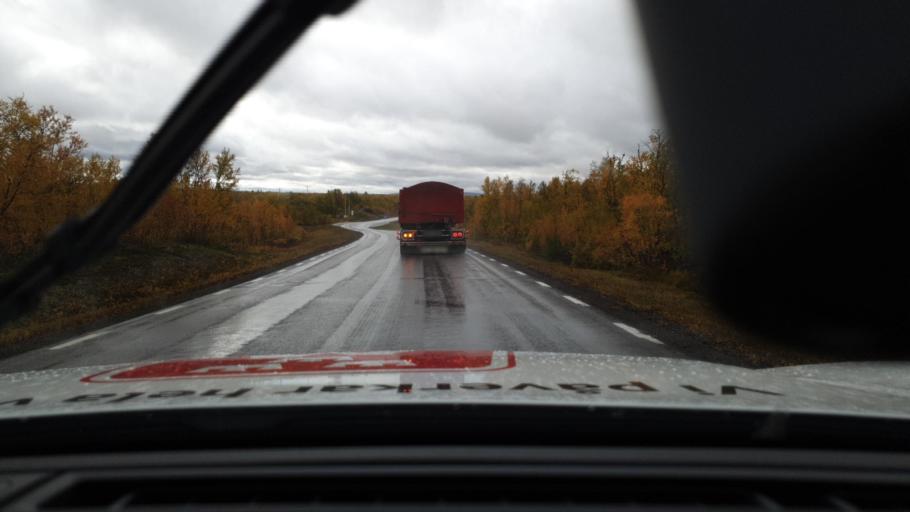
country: SE
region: Norrbotten
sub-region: Kiruna Kommun
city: Kiruna
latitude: 67.7886
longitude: 20.2295
